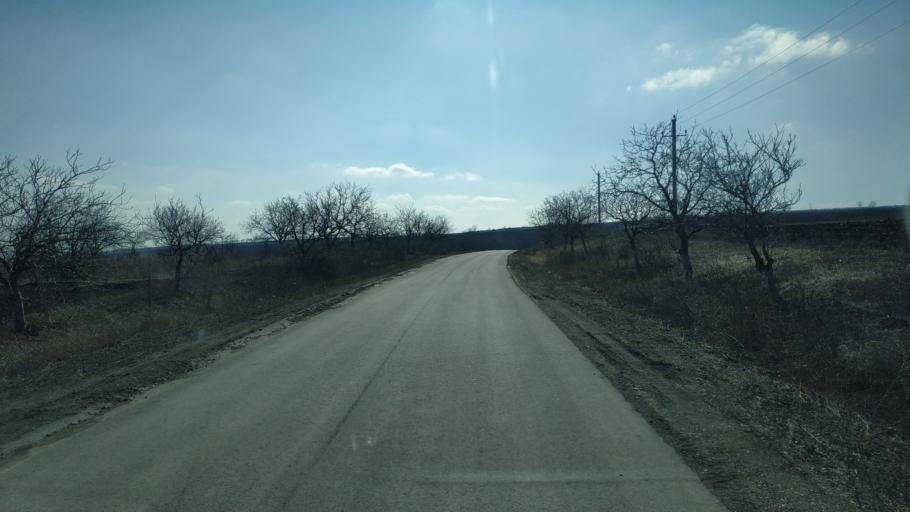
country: MD
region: Hincesti
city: Hincesti
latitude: 46.7692
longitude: 28.6786
